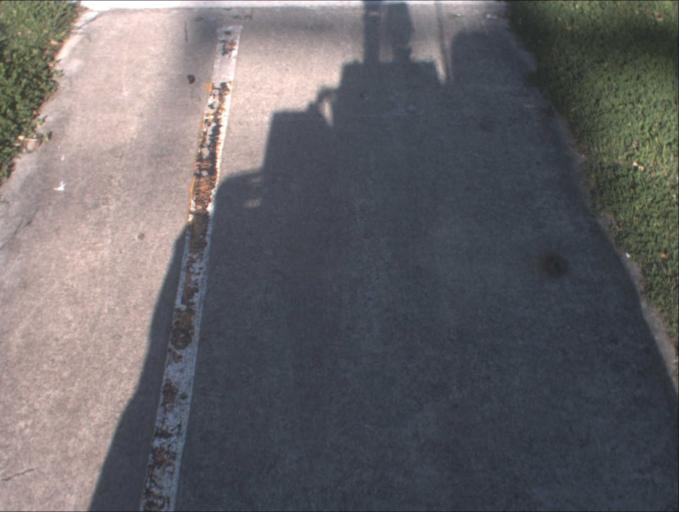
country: AU
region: Queensland
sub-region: Logan
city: Chambers Flat
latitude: -27.7655
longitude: 153.1063
